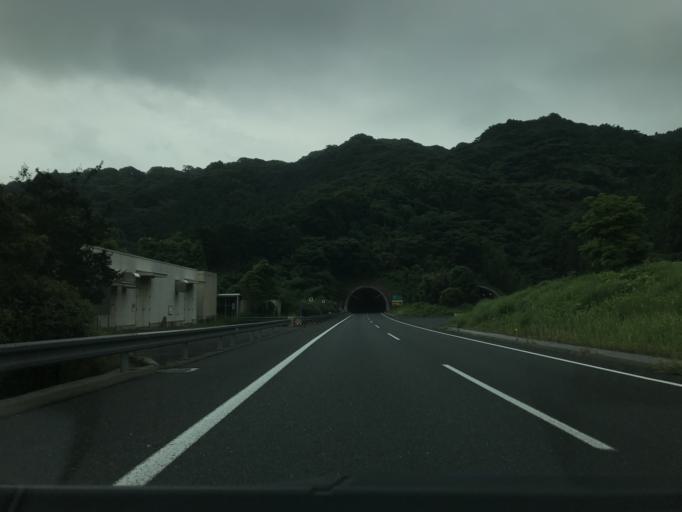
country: JP
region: Fukuoka
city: Kitakyushu
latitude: 33.8141
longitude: 130.9058
